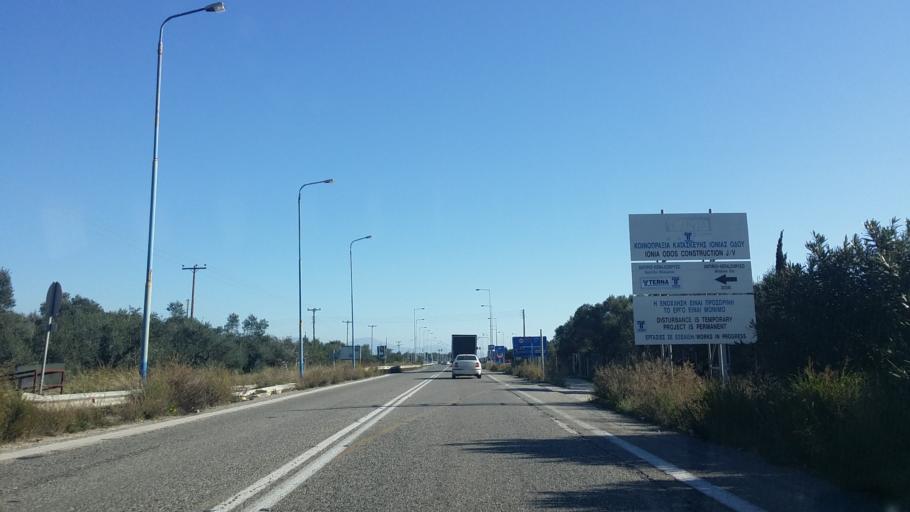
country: GR
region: West Greece
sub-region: Nomos Aitolias kai Akarnanias
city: Antirrio
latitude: 38.3386
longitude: 21.7511
